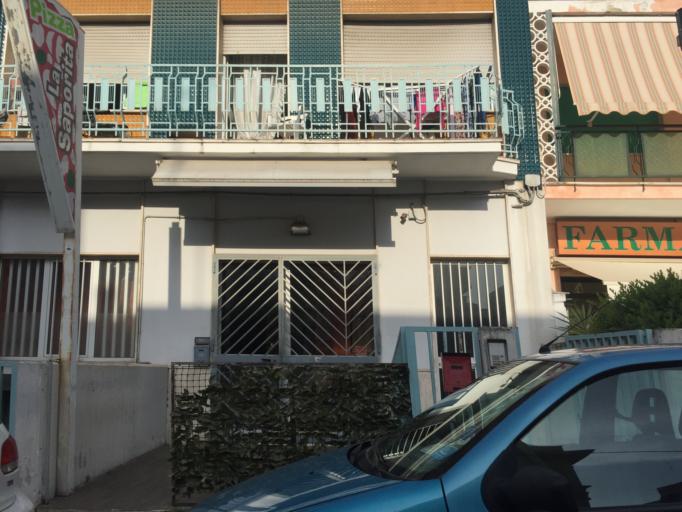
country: IT
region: Apulia
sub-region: Provincia di Bari
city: Capurso
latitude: 41.0465
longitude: 16.9189
